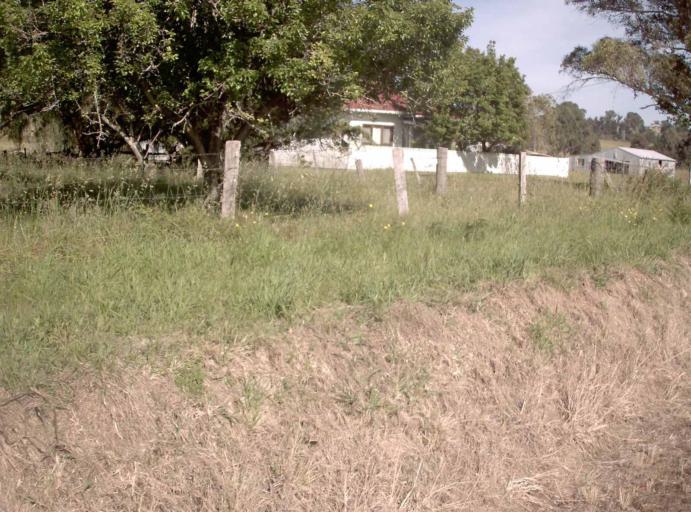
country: AU
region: Victoria
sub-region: East Gippsland
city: Bairnsdale
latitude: -37.7315
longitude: 147.8106
